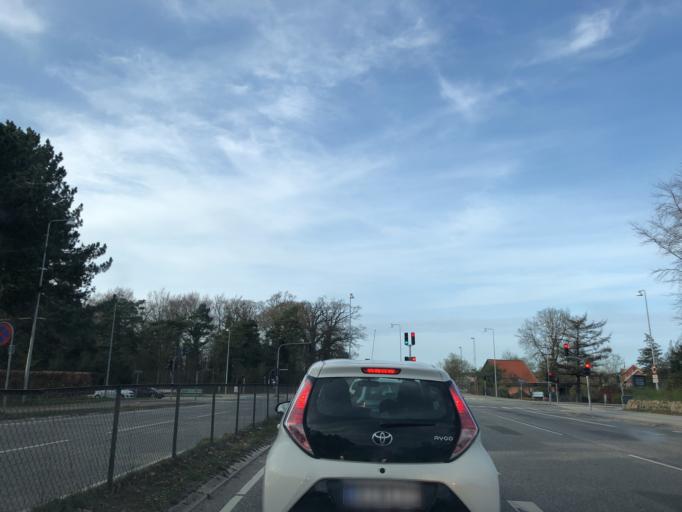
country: DK
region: Zealand
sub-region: Koge Kommune
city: Koge
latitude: 55.4559
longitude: 12.1730
